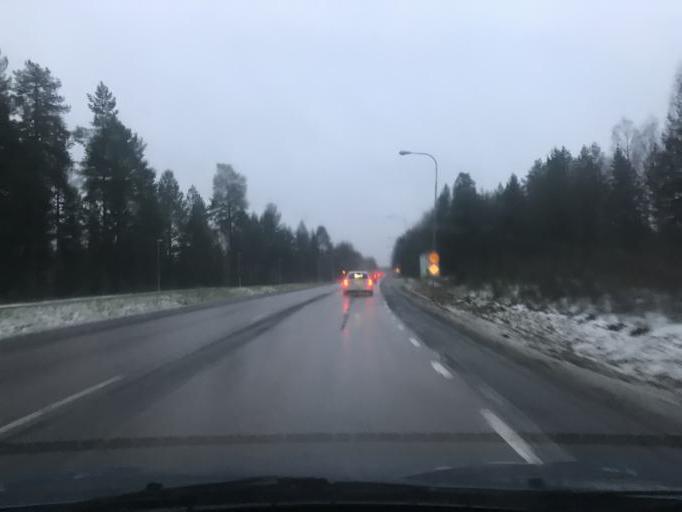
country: SE
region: Norrbotten
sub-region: Lulea Kommun
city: Gammelstad
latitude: 65.6293
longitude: 22.0374
